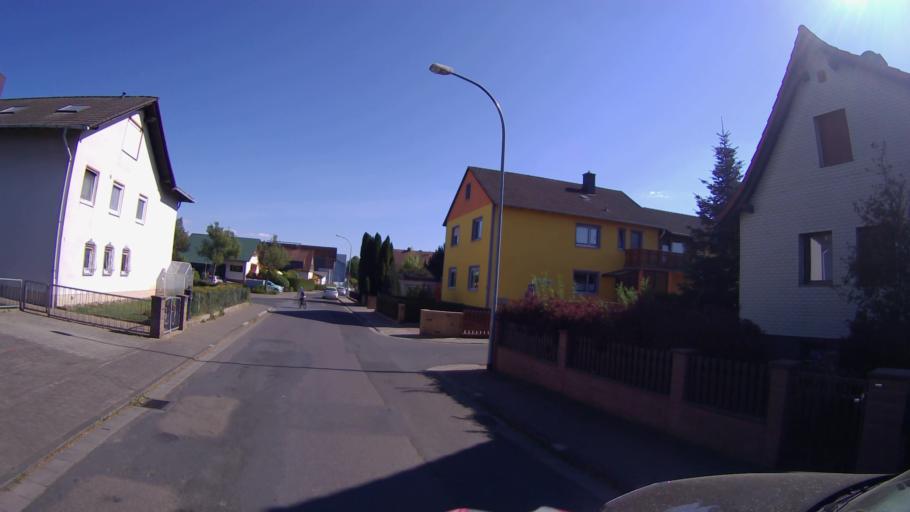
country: DE
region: Hesse
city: Hain-Grundau
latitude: 50.2002
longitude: 9.1161
